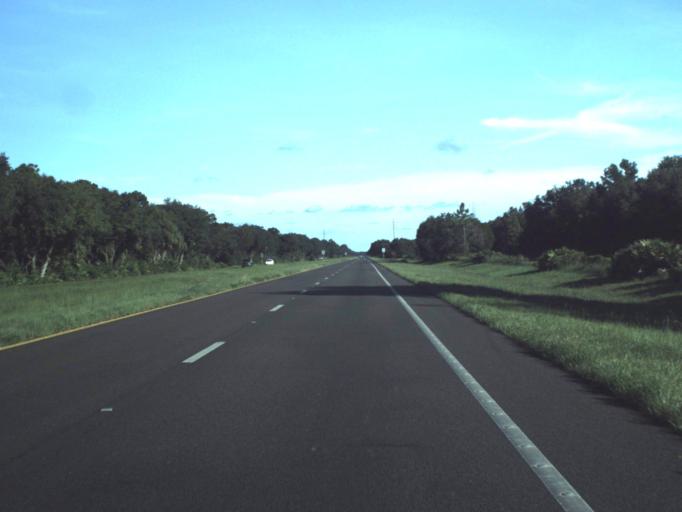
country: US
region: Florida
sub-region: Levy County
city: Inglis
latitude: 29.0006
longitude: -82.6555
